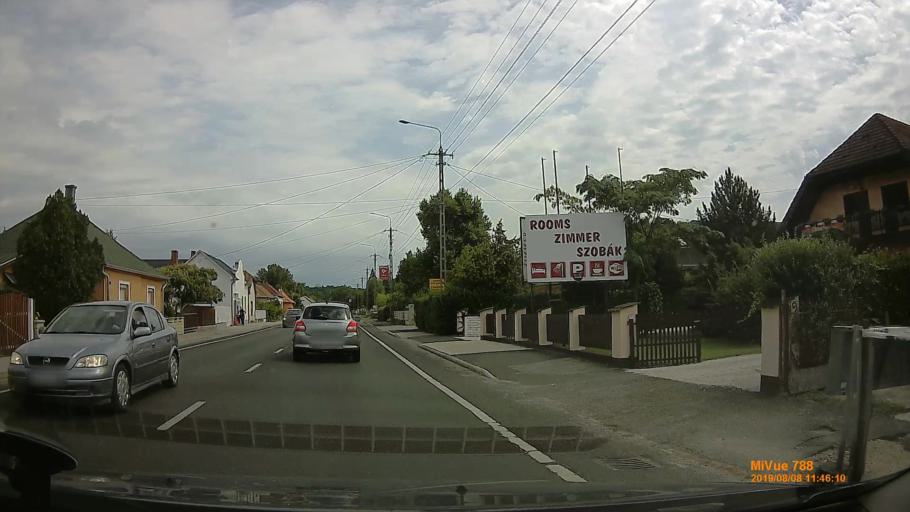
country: HU
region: Somogy
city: Balatonboglar
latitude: 46.7738
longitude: 17.6416
